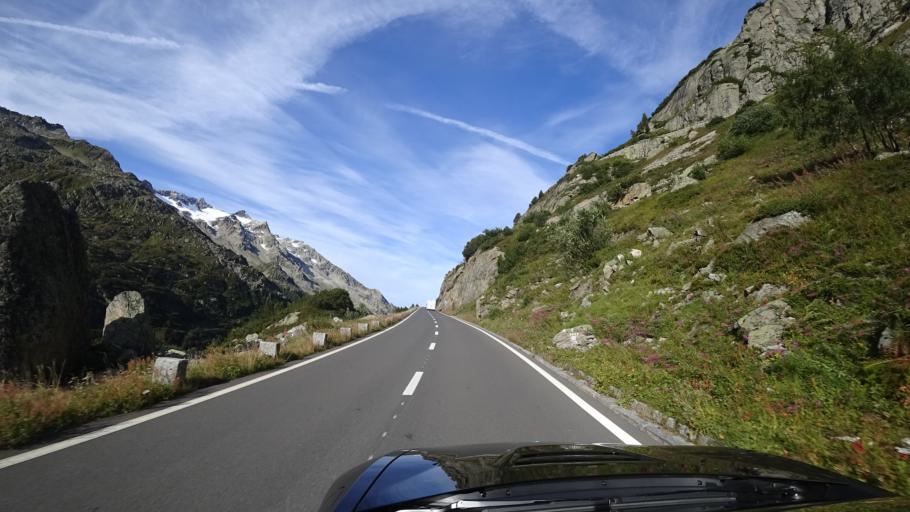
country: CH
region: Obwalden
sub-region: Obwalden
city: Engelberg
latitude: 46.7325
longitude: 8.4210
